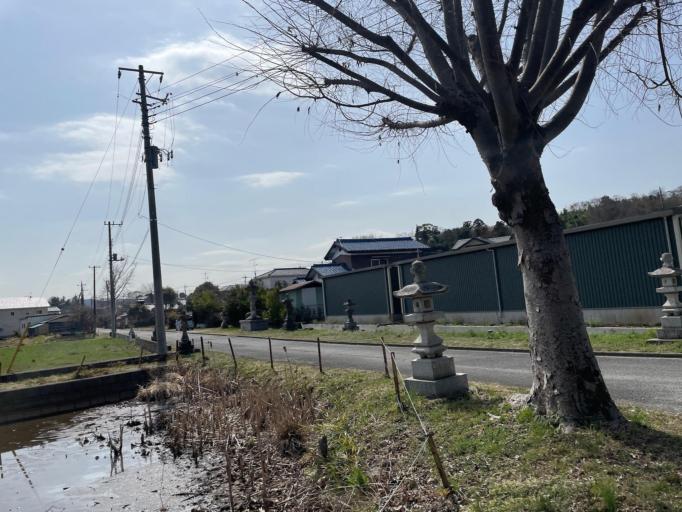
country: JP
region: Saitama
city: Ogawa
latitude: 36.0819
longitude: 139.2886
